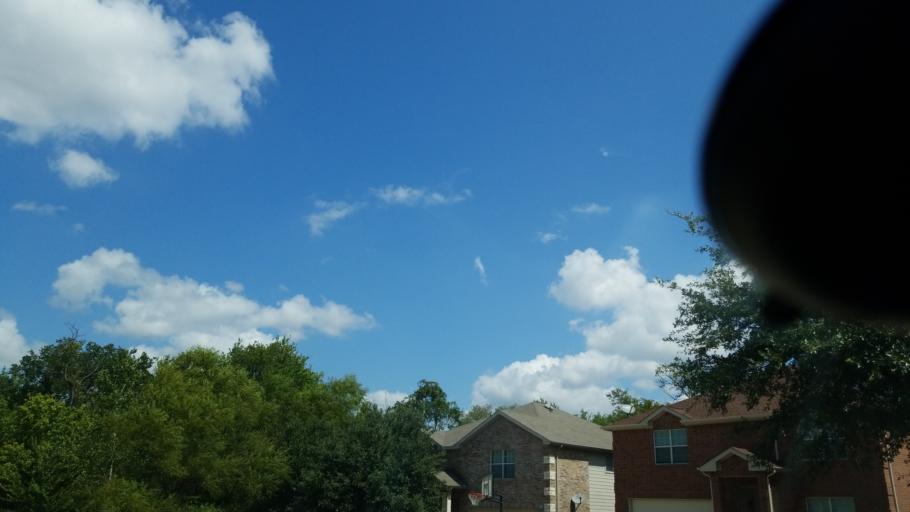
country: US
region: Texas
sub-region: Dallas County
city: Grand Prairie
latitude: 32.7268
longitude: -96.9878
